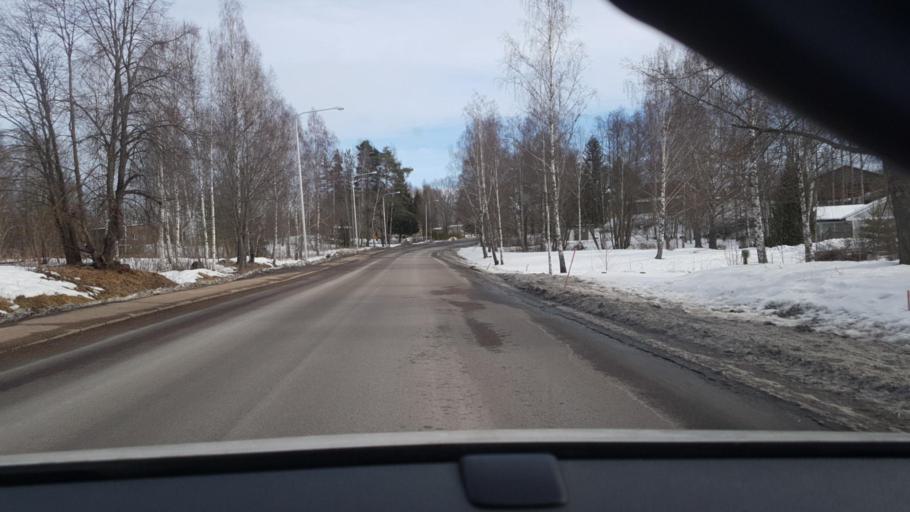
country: SE
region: Vaermland
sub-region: Arvika Kommun
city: Arvika
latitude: 59.6741
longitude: 12.4957
